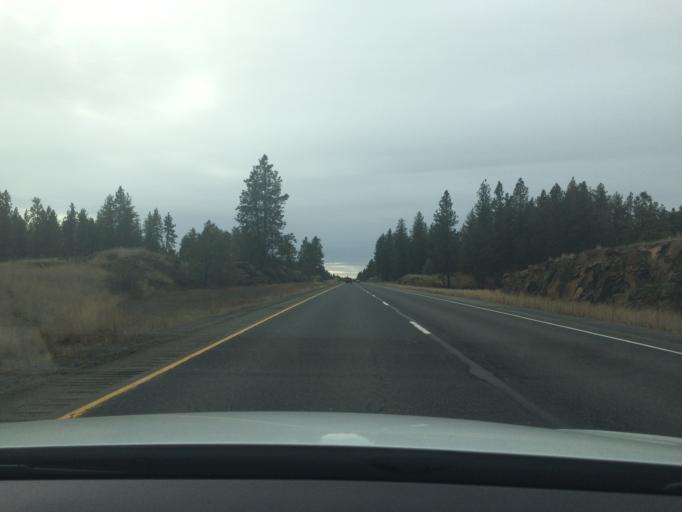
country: US
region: Washington
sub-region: Spokane County
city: Medical Lake
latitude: 47.5243
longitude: -117.6638
